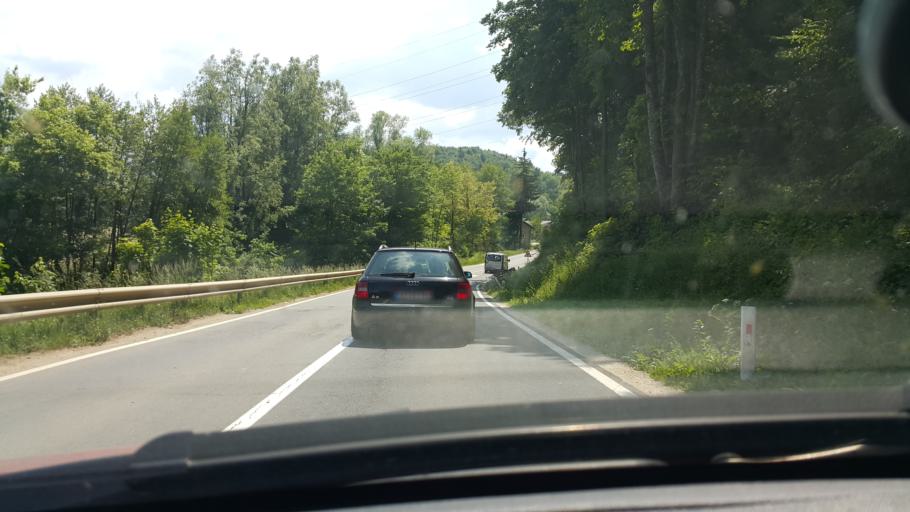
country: SI
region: Novo Mesto
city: Novo Mesto
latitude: 45.7808
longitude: 15.1777
